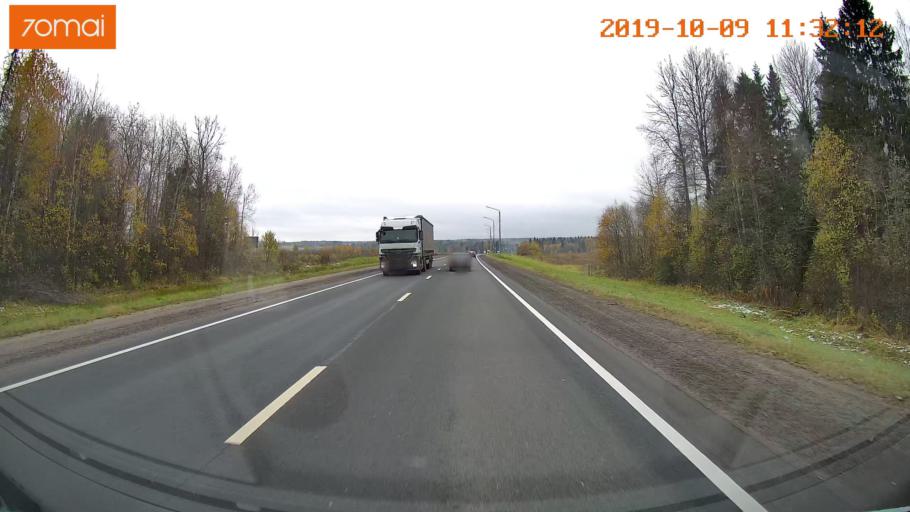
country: RU
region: Vologda
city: Gryazovets
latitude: 59.0382
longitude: 40.1064
